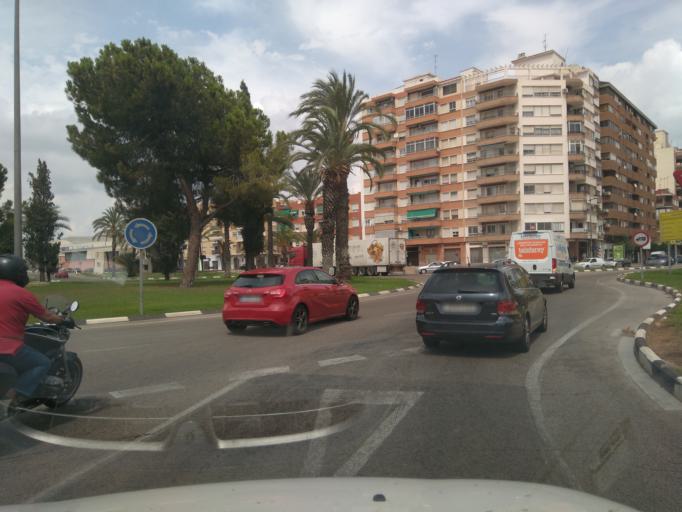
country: ES
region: Valencia
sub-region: Provincia de Valencia
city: Alzira
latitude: 39.1475
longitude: -0.4406
